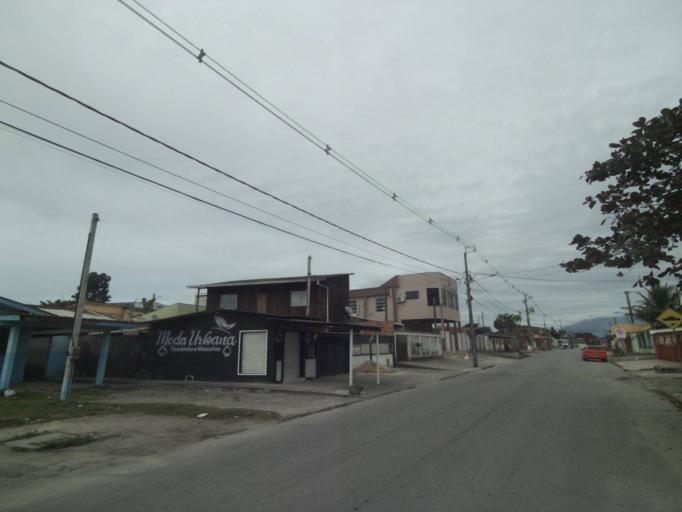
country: BR
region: Parana
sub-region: Paranagua
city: Paranagua
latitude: -25.5160
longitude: -48.5315
